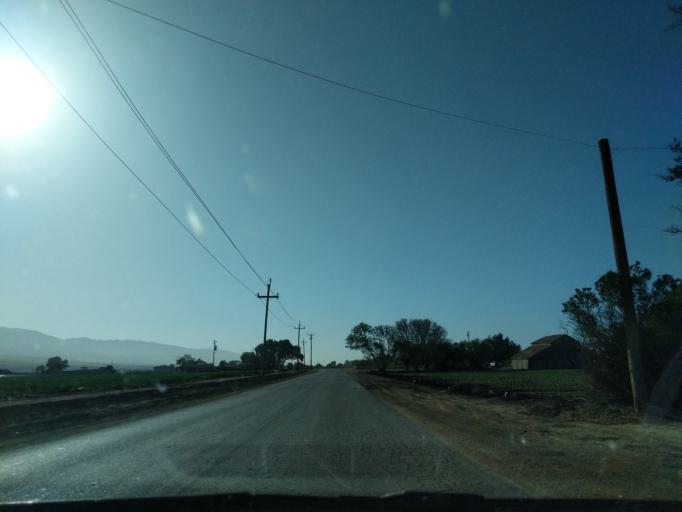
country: US
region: California
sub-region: Monterey County
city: Soledad
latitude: 36.3997
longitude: -121.3391
